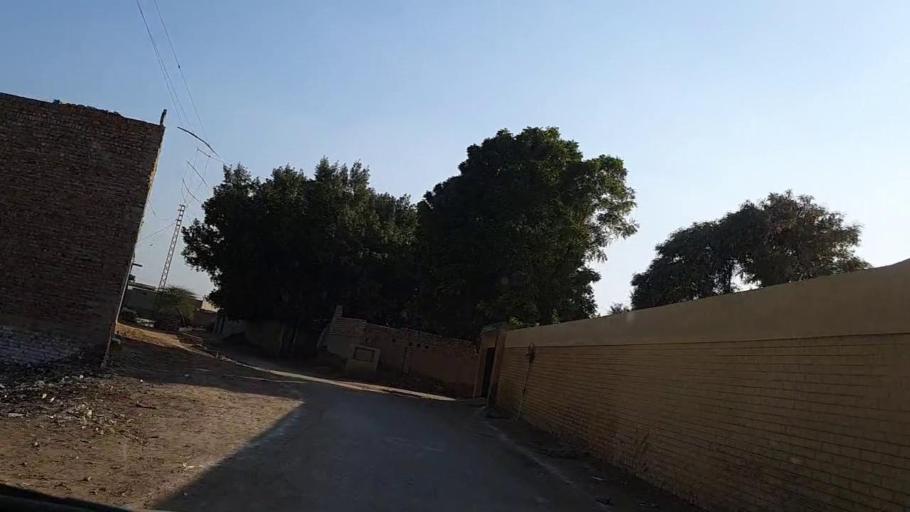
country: PK
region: Sindh
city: Sakrand
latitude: 26.1290
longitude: 68.2191
